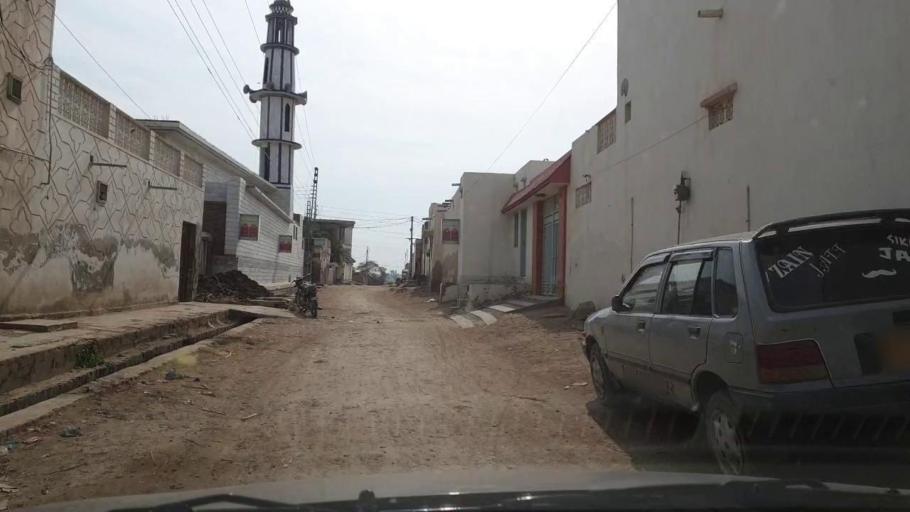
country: PK
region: Sindh
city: Sinjhoro
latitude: 26.1055
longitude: 68.8286
